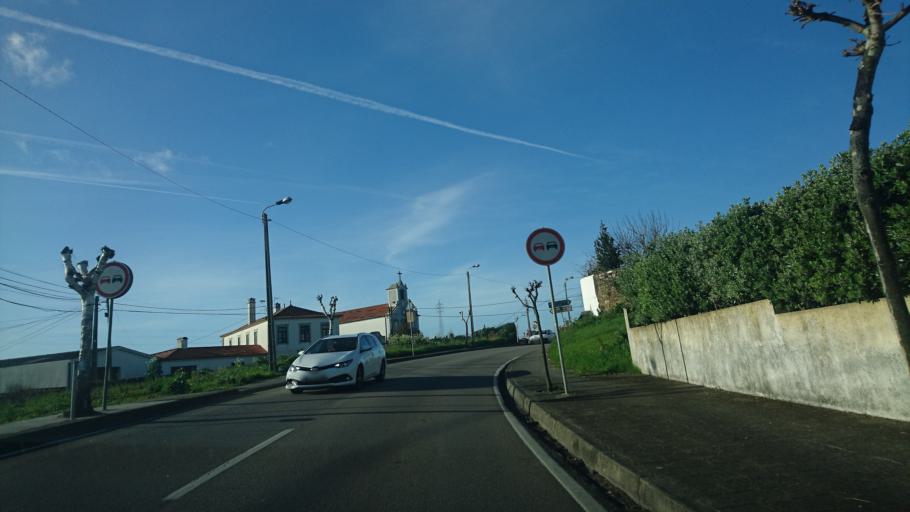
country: PT
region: Aveiro
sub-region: Espinho
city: Souto
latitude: 40.9775
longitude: -8.6315
